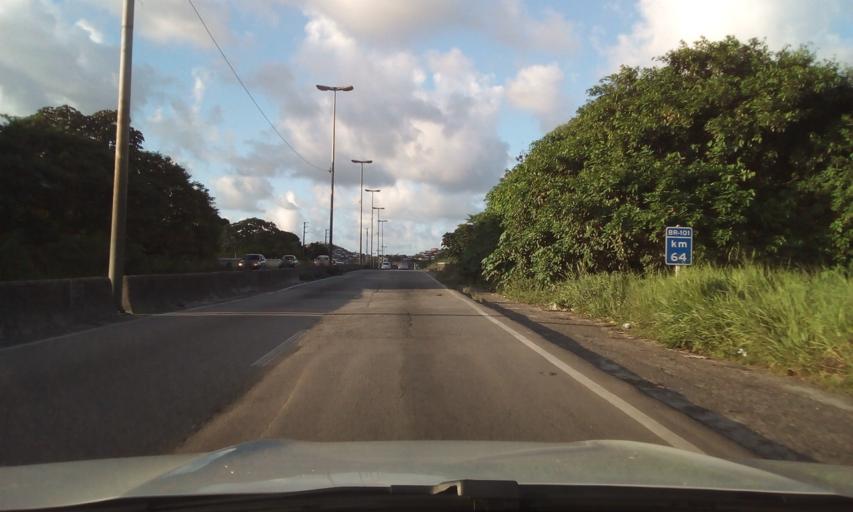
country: BR
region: Pernambuco
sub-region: Recife
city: Recife
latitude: -8.0175
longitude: -34.9413
